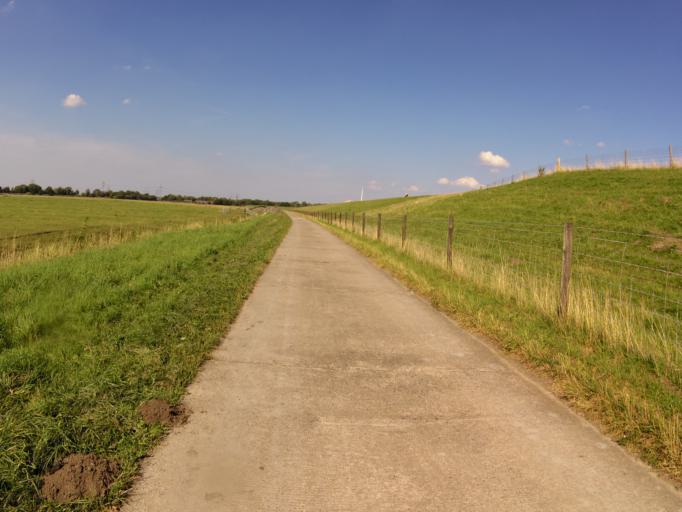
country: DE
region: Lower Saxony
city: Nordenham
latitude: 53.4140
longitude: 8.4718
